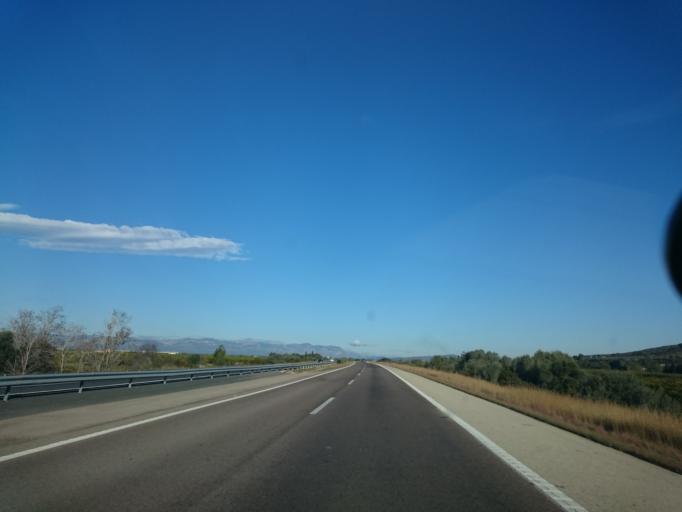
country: ES
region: Valencia
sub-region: Provincia de Castello
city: Vinaros
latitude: 40.5038
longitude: 0.4159
